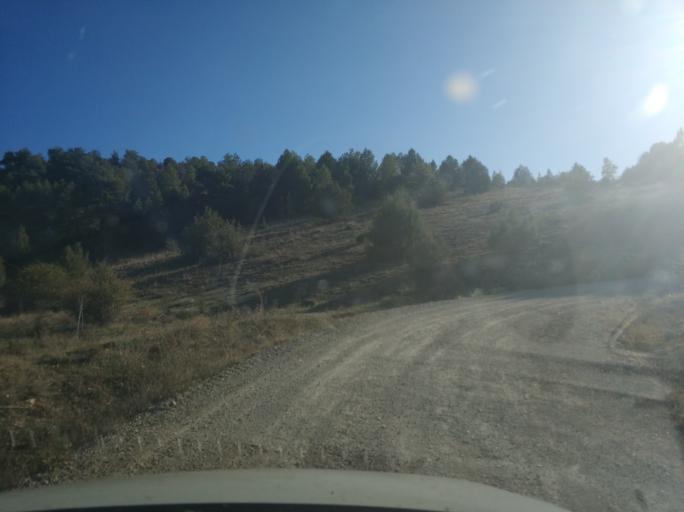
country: ES
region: Castille and Leon
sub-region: Provincia de Burgos
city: Hontoria del Pinar
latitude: 41.8424
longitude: -3.1624
